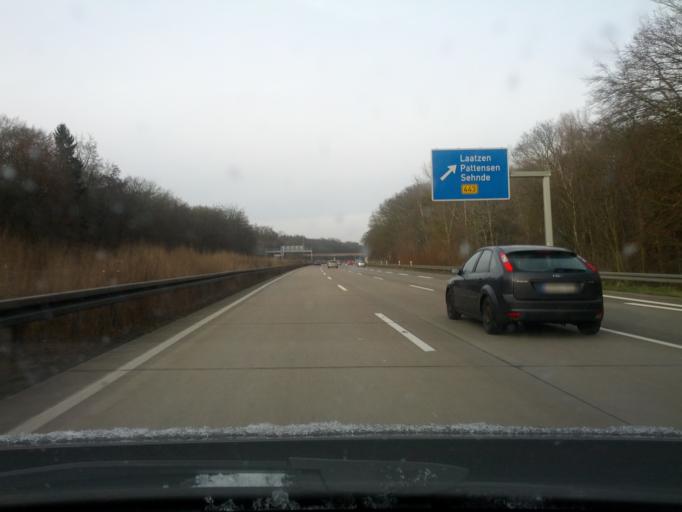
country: DE
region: Lower Saxony
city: Sarstedt
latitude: 52.3061
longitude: 9.8743
